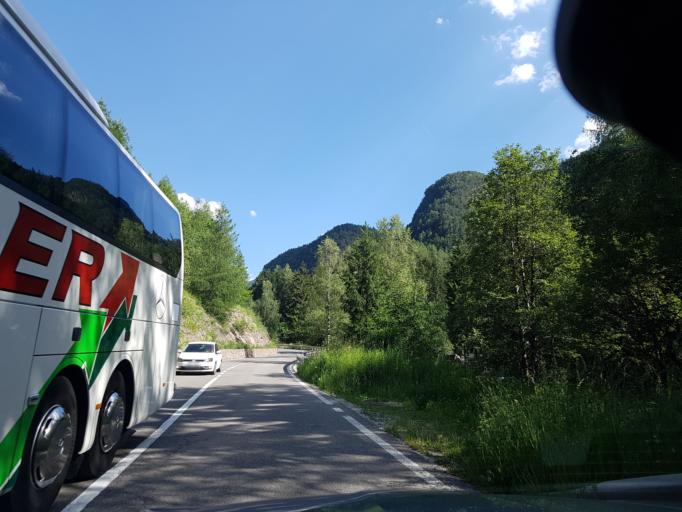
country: IT
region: Trentino-Alto Adige
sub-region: Bolzano
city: Ortisei
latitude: 46.5884
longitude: 11.6277
